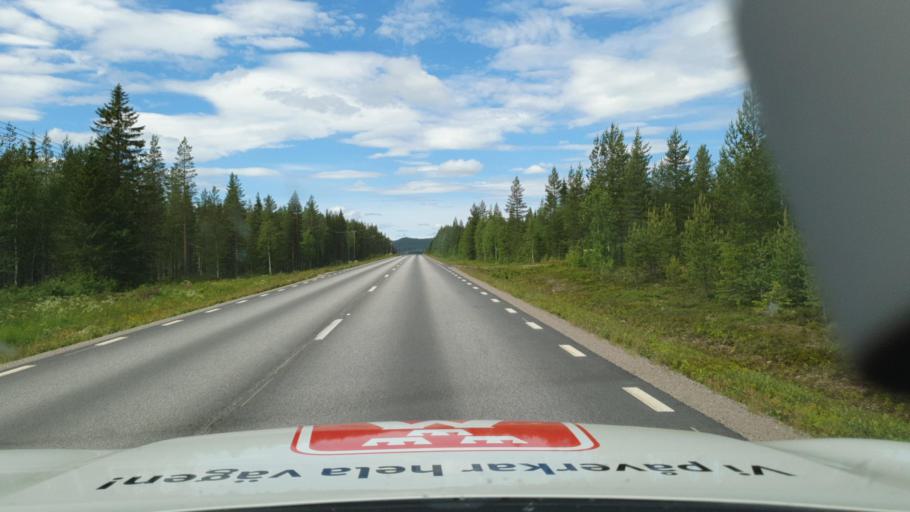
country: SE
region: Vaesterbotten
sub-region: Norsjo Kommun
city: Norsjoe
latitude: 65.2424
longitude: 19.7096
